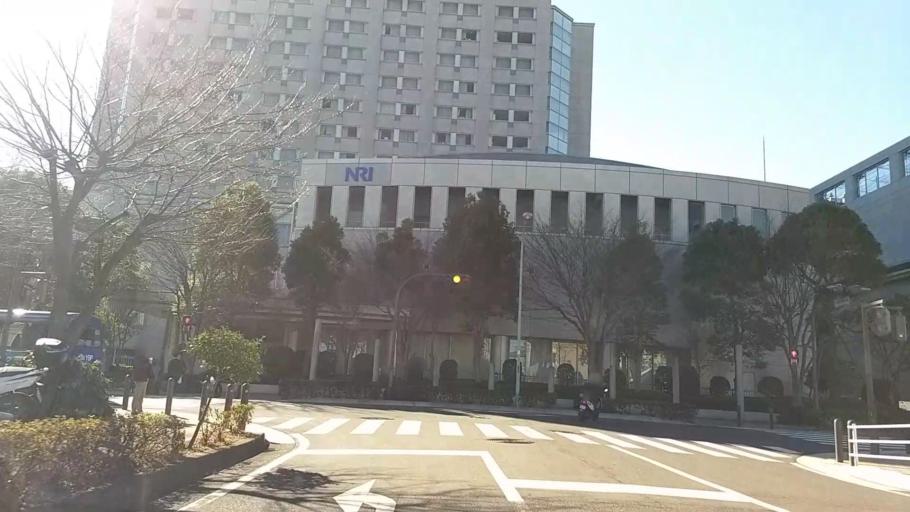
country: JP
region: Kanagawa
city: Yokohama
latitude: 35.4544
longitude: 139.5964
